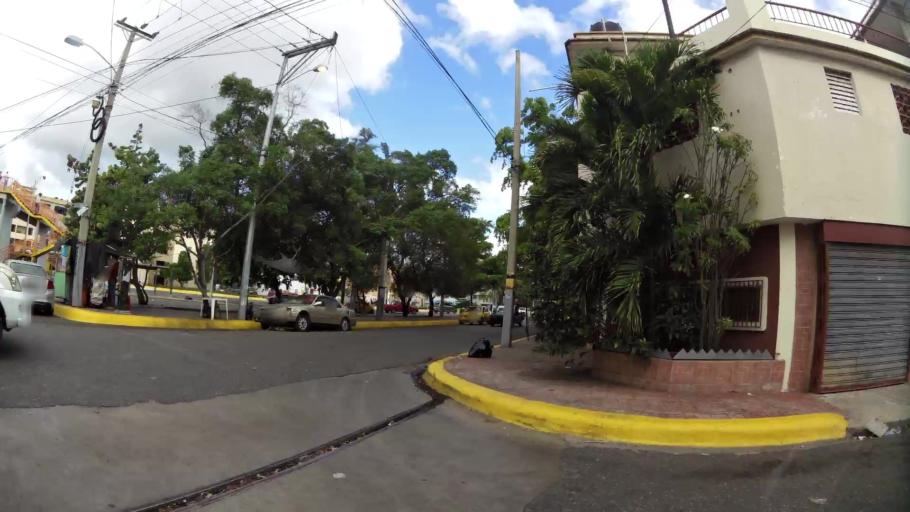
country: DO
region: Nacional
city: San Carlos
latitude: 18.4833
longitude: -69.9045
